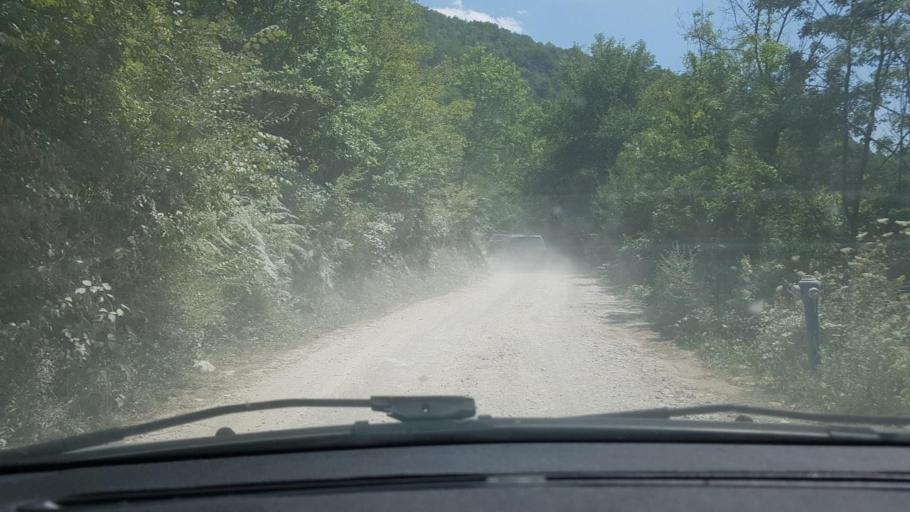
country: BA
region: Federation of Bosnia and Herzegovina
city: Orasac
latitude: 44.6542
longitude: 16.0314
